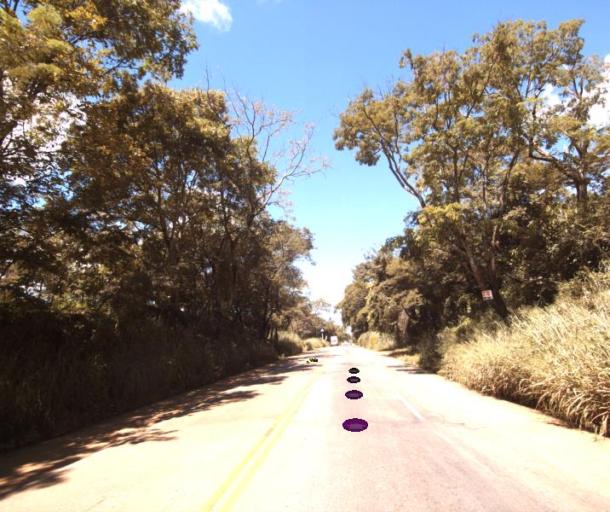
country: BR
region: Goias
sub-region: Anapolis
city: Anapolis
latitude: -16.1058
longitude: -49.0306
